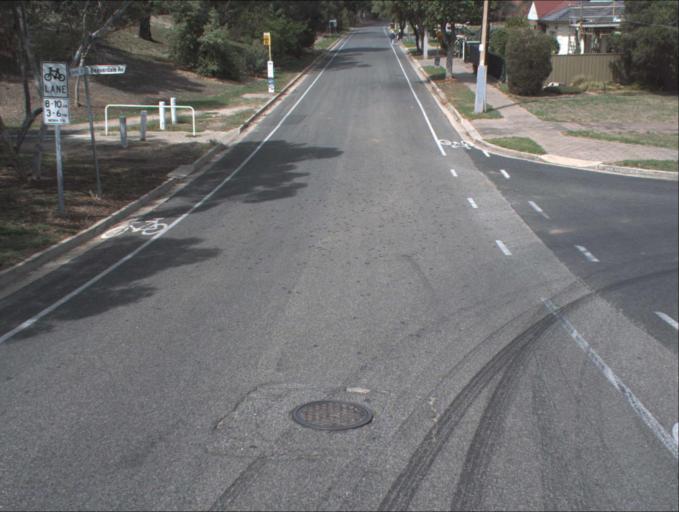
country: AU
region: South Australia
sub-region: Campbelltown
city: Paradise
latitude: -34.8632
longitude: 138.6663
